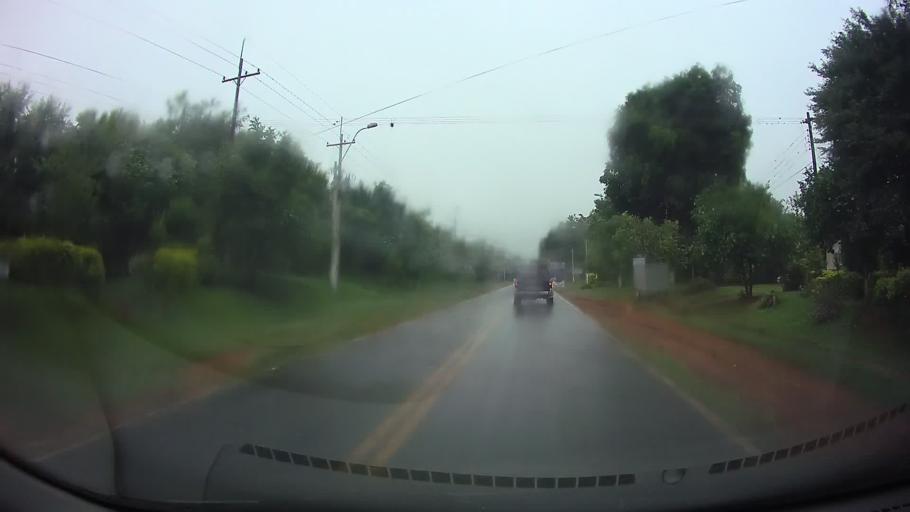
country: PY
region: Central
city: Ita
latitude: -25.4719
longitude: -57.3639
